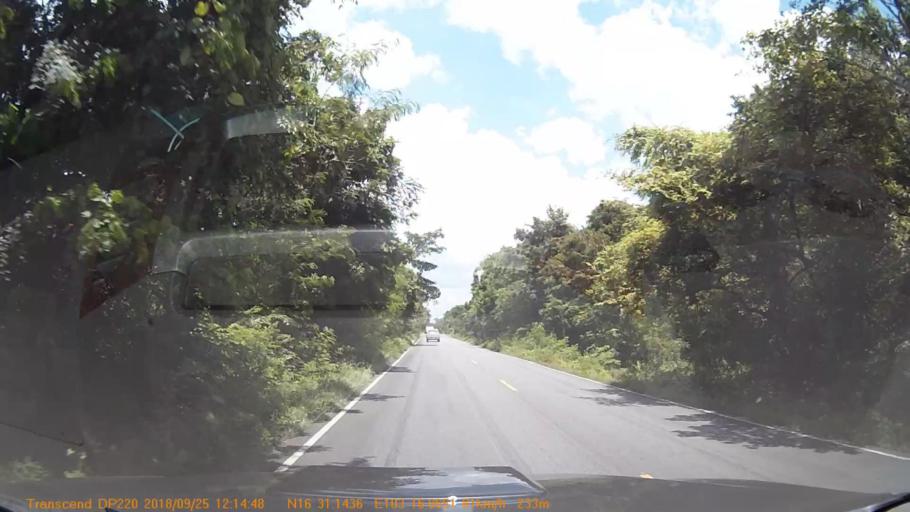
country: TH
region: Kalasin
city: Huai Mek
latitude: 16.5192
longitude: 103.2678
